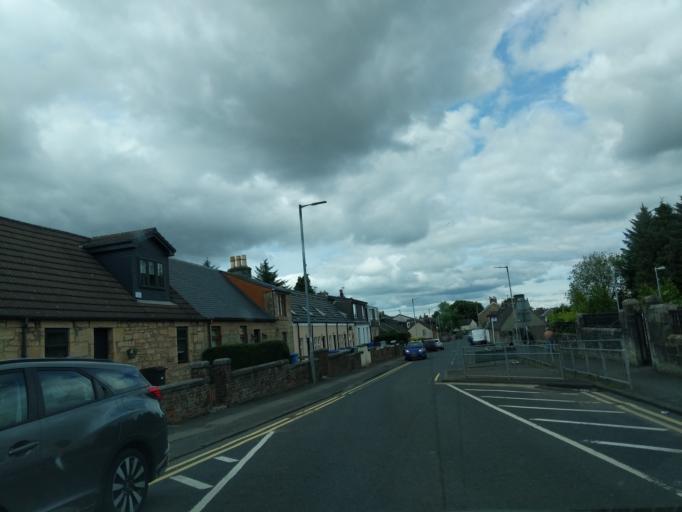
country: GB
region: Scotland
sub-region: South Lanarkshire
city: Stonehouse
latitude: 55.6958
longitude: -3.9868
